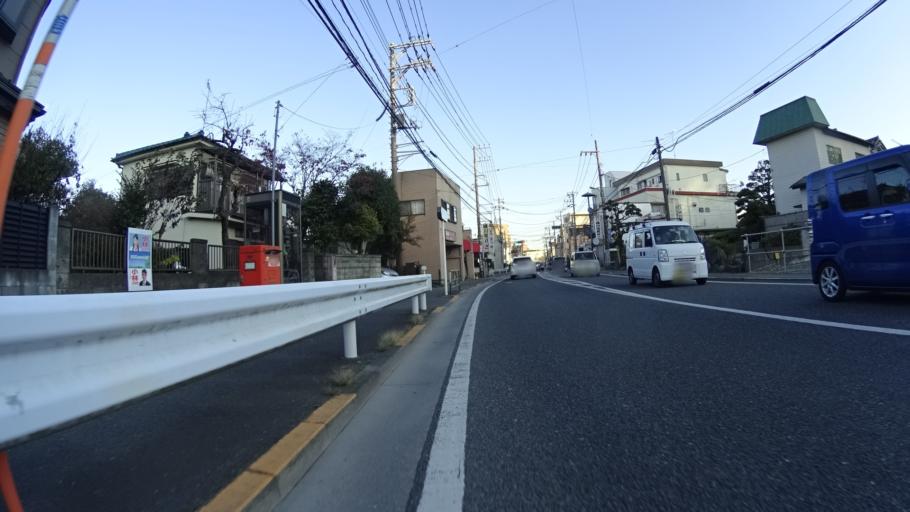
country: JP
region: Tokyo
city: Hachioji
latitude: 35.6634
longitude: 139.3080
